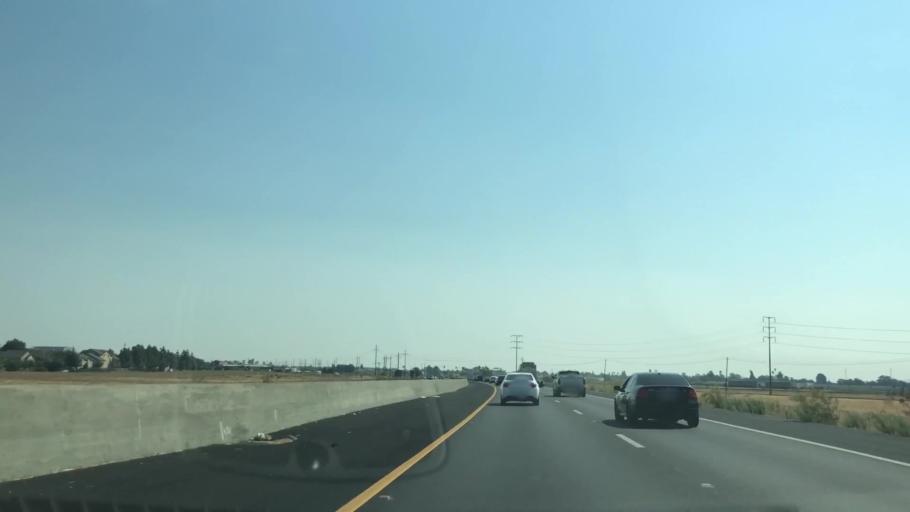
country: US
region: California
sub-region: Solano County
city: Suisun
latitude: 38.2406
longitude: -122.0566
